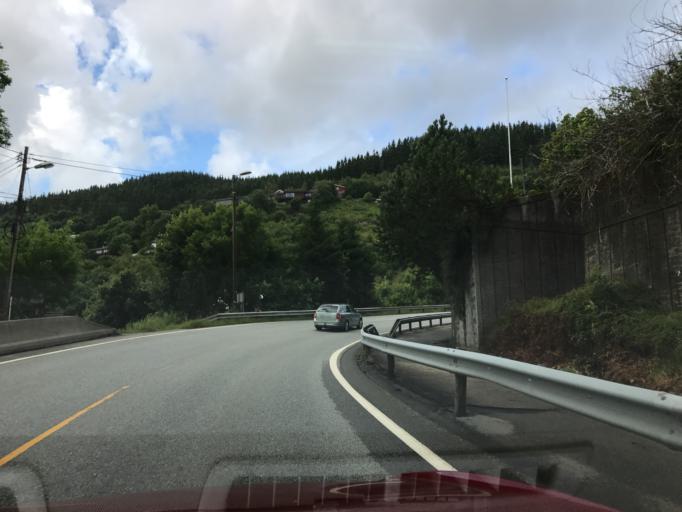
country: NO
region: Hordaland
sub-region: Os
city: Syfteland
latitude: 60.2902
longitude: 5.3842
